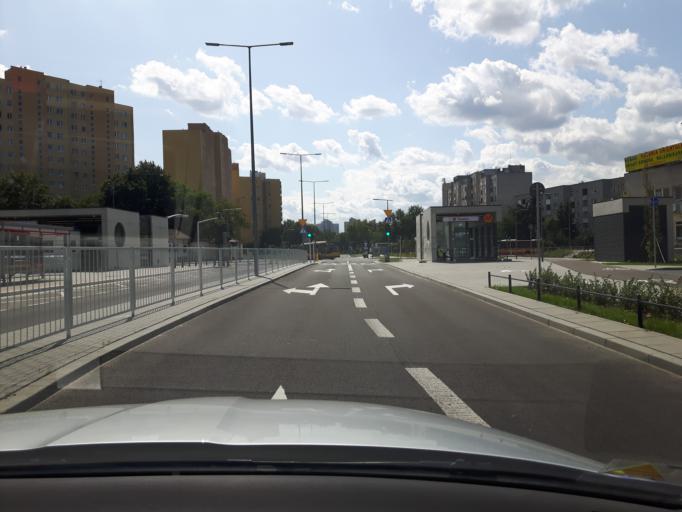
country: PL
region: Masovian Voivodeship
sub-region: Warszawa
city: Targowek
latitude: 52.2759
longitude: 21.0565
